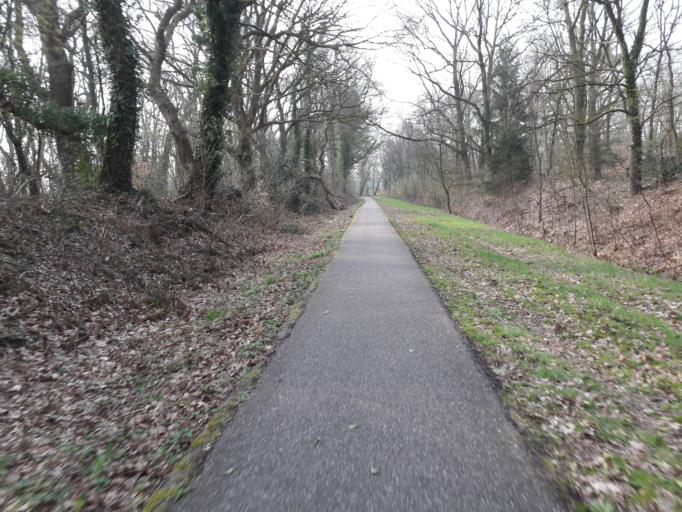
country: NL
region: Drenthe
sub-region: Gemeente Aa en Hunze
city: Anloo
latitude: 52.9410
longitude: 6.6668
